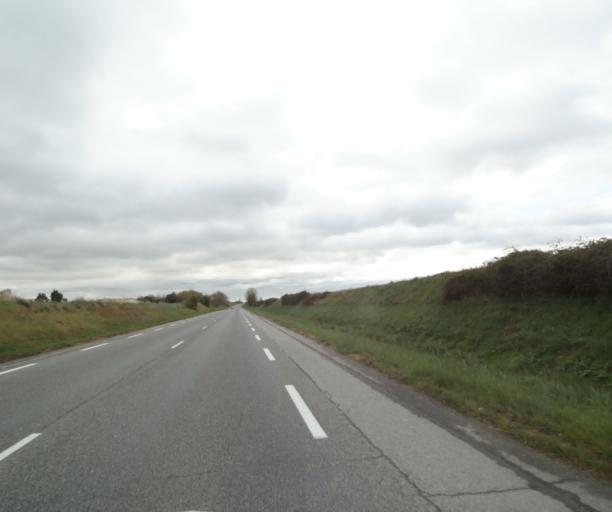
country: FR
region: Midi-Pyrenees
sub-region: Departement de l'Ariege
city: Saverdun
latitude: 43.2376
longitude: 1.5916
